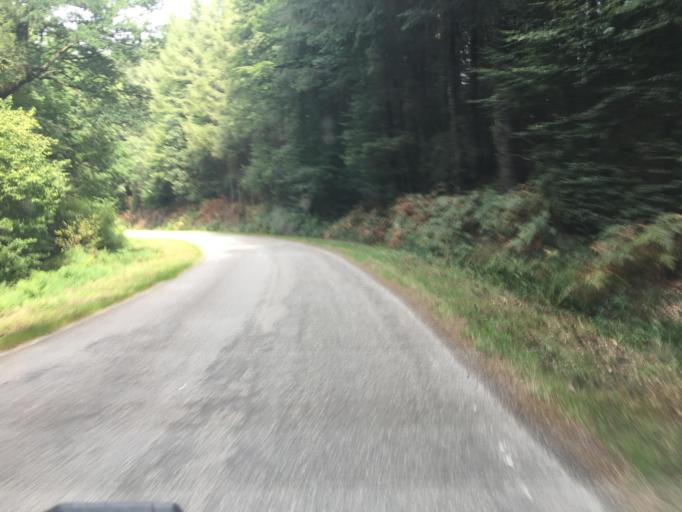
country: FR
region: Brittany
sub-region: Departement des Cotes-d'Armor
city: Gouarec
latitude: 48.2026
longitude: -3.1163
